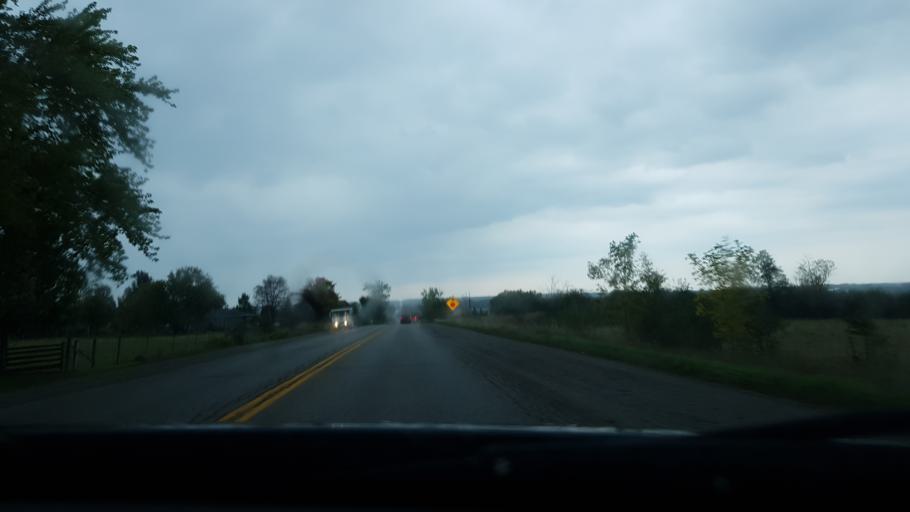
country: CA
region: Ontario
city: Omemee
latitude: 44.3833
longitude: -78.6039
